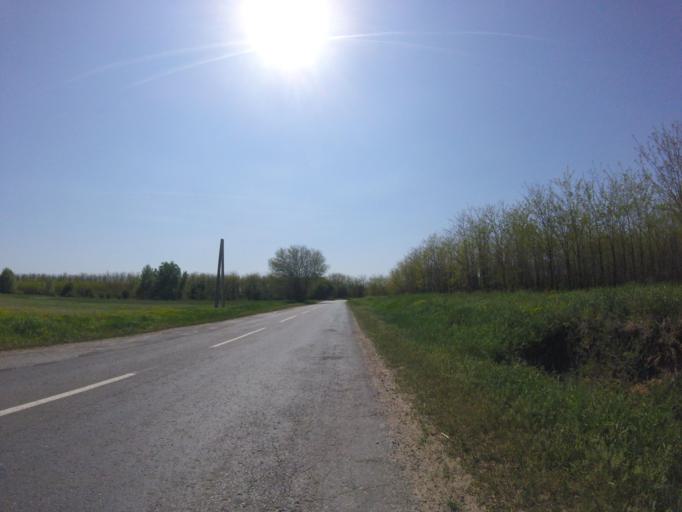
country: HU
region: Pest
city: Ujhartyan
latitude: 47.2357
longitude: 19.4453
